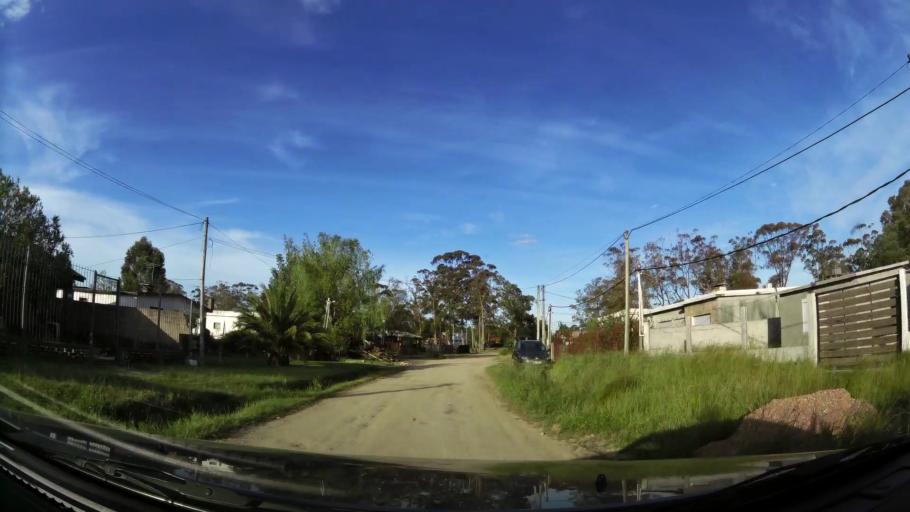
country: UY
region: Canelones
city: Atlantida
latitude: -34.7710
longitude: -55.8423
